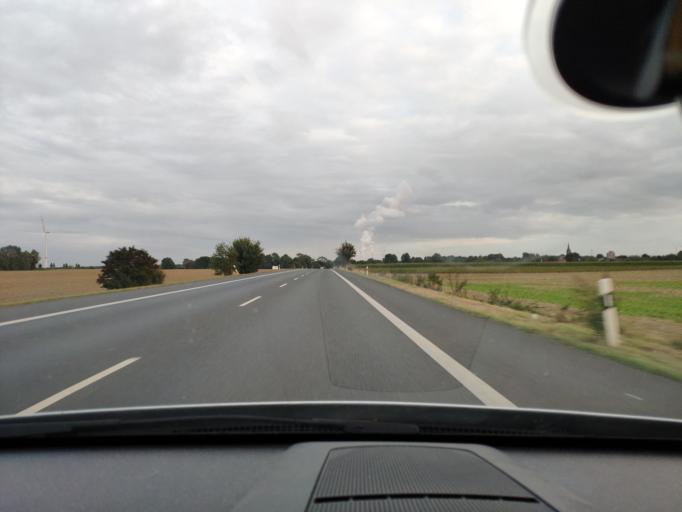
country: DE
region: North Rhine-Westphalia
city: Siersdorf
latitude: 50.9144
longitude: 6.2531
